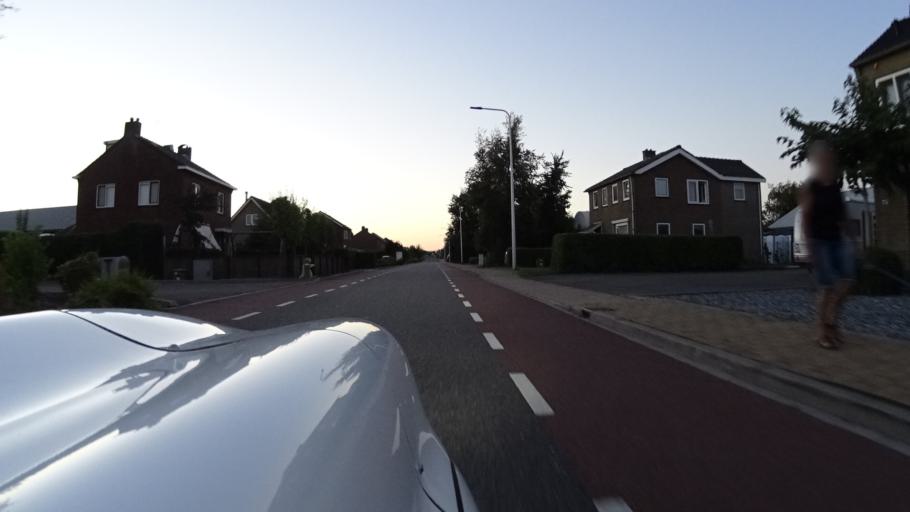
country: NL
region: South Holland
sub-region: Gemeente Kaag en Braassem
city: Oude Wetering
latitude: 52.1910
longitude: 4.6202
